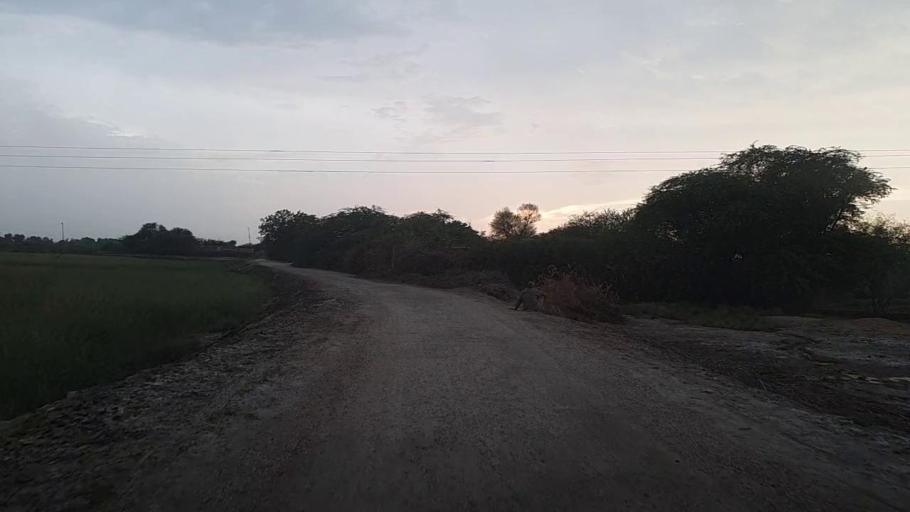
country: PK
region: Sindh
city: Karaundi
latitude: 27.0136
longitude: 68.3474
